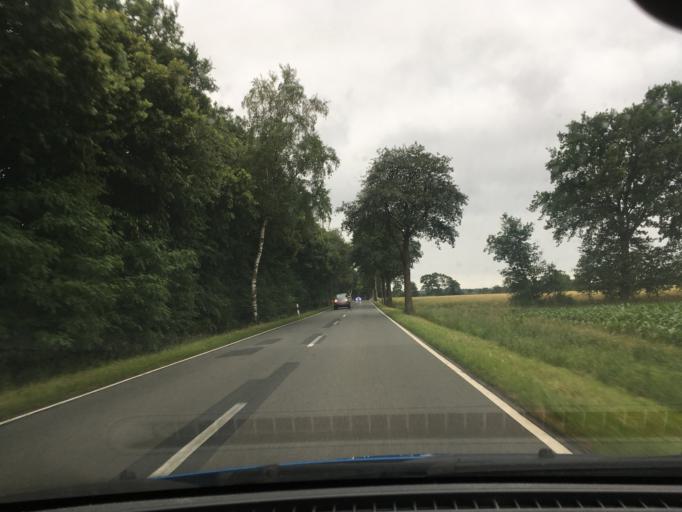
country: DE
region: Lower Saxony
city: Egestorf
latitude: 53.2047
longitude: 10.0689
